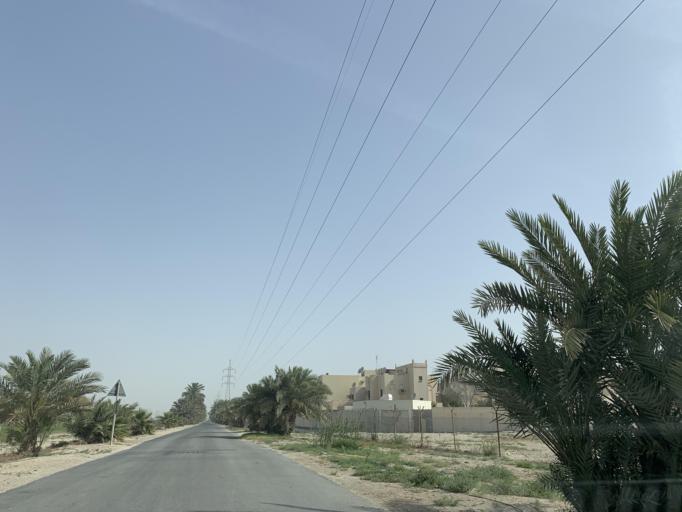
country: BH
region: Northern
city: Madinat `Isa
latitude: 26.1683
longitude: 50.5359
